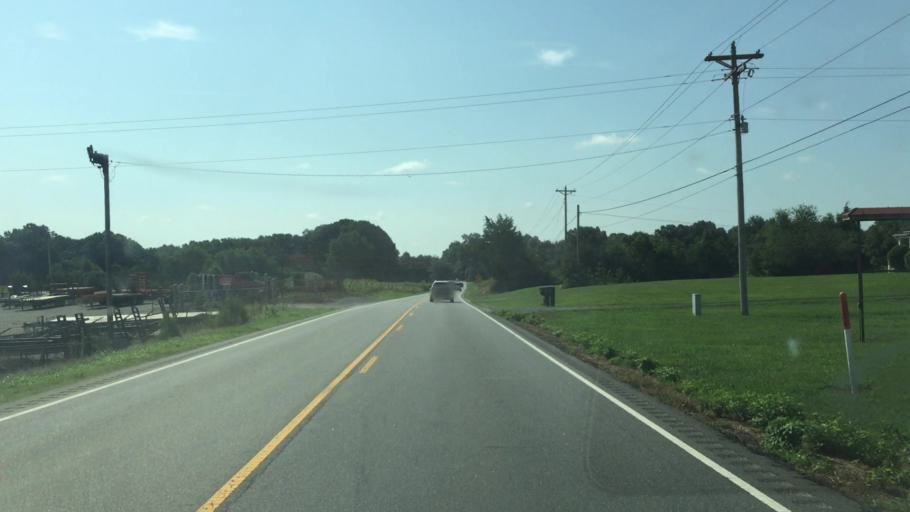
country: US
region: North Carolina
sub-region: Union County
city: Fairview
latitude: 35.1569
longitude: -80.5637
